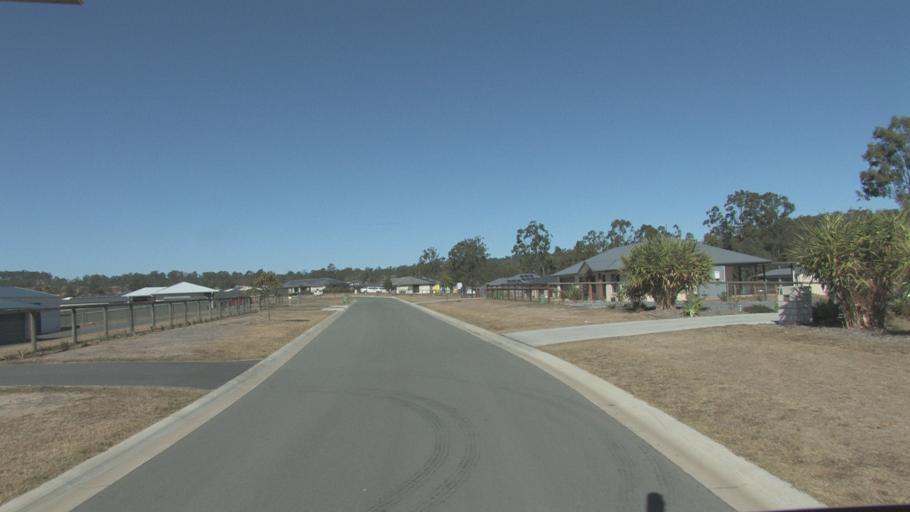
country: AU
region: Queensland
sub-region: Logan
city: Cedar Vale
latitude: -27.8674
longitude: 153.0424
